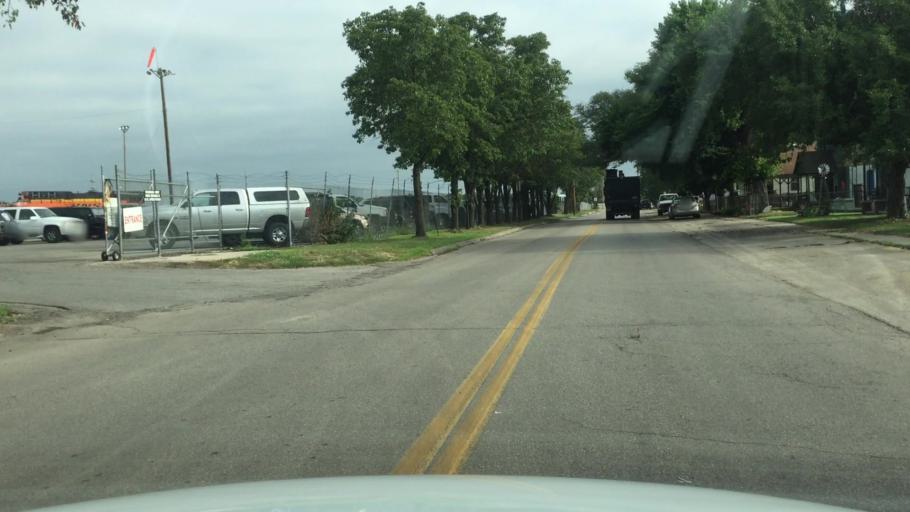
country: US
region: Kansas
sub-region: Shawnee County
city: Topeka
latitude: 39.0592
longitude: -95.6556
